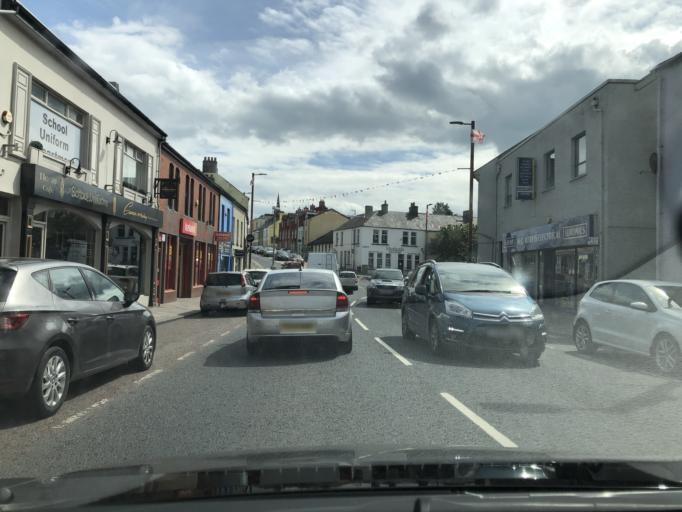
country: GB
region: Northern Ireland
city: Ballynahinch
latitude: 54.4013
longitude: -5.8973
